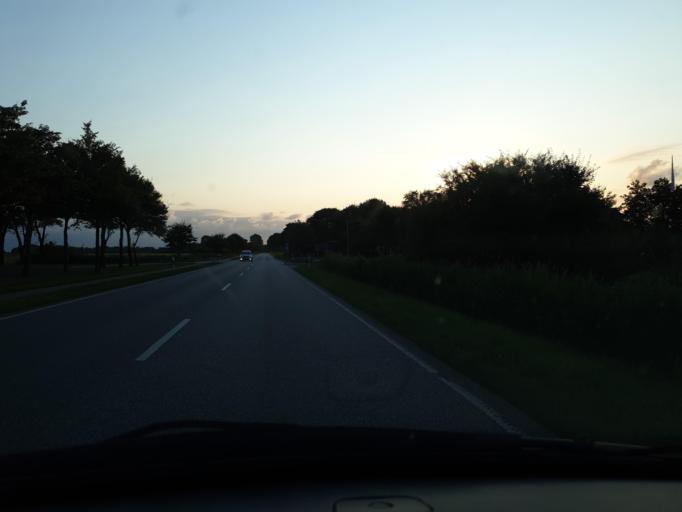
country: DE
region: Schleswig-Holstein
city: Schmedeswurth
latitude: 53.9071
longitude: 9.0769
